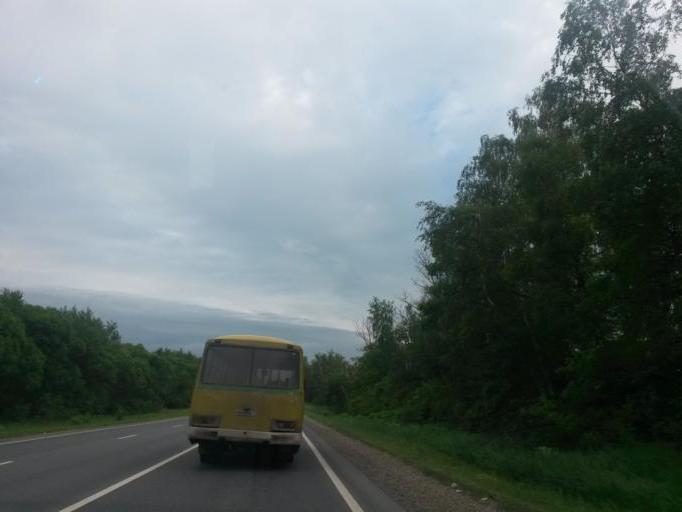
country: RU
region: Moskovskaya
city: Barybino
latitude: 55.2237
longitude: 37.8673
